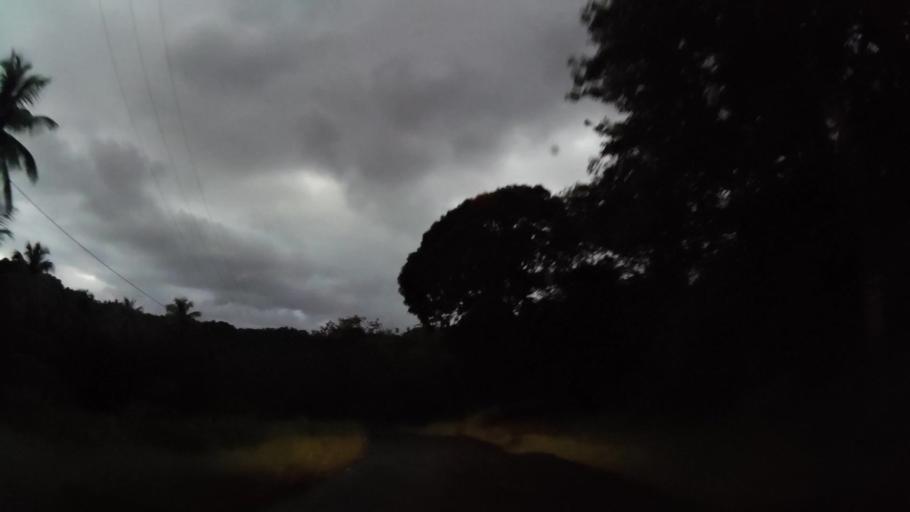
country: DM
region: Saint Andrew
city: Calibishie
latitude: 15.5851
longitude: -61.3371
